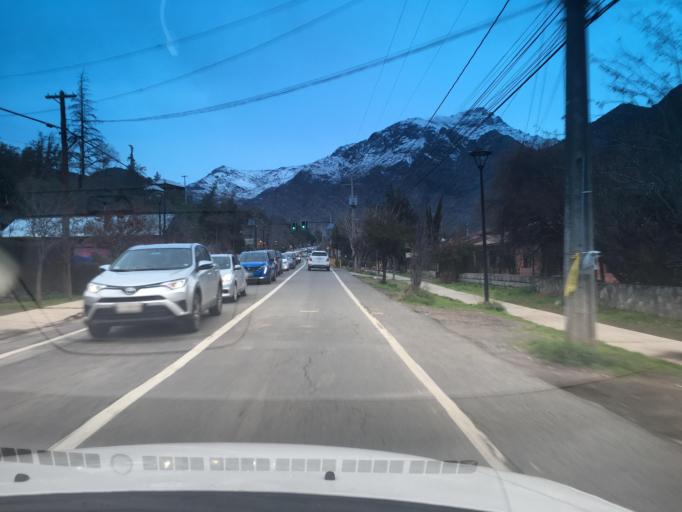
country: CL
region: Santiago Metropolitan
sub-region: Provincia de Cordillera
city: Puente Alto
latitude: -33.6986
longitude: -70.3344
